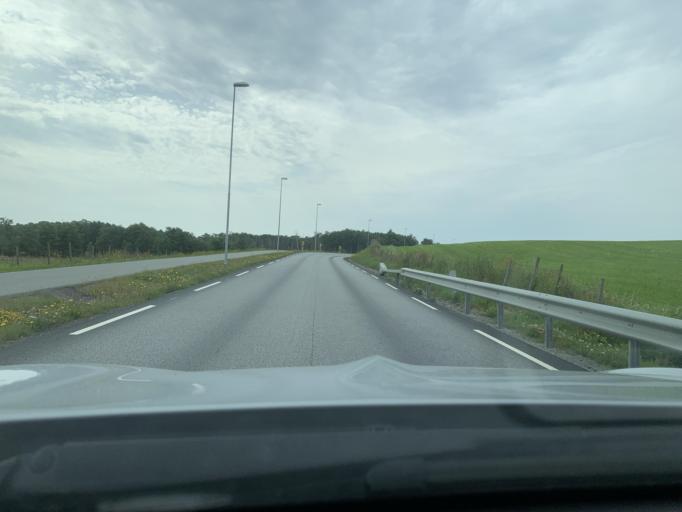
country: NO
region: Rogaland
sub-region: Time
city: Bryne
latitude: 58.7649
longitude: 5.7151
